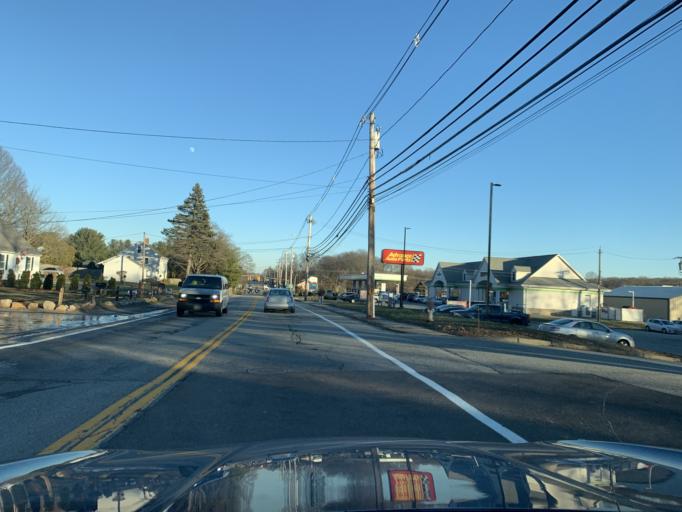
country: US
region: Rhode Island
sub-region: Kent County
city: West Warwick
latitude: 41.6964
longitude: -71.5043
